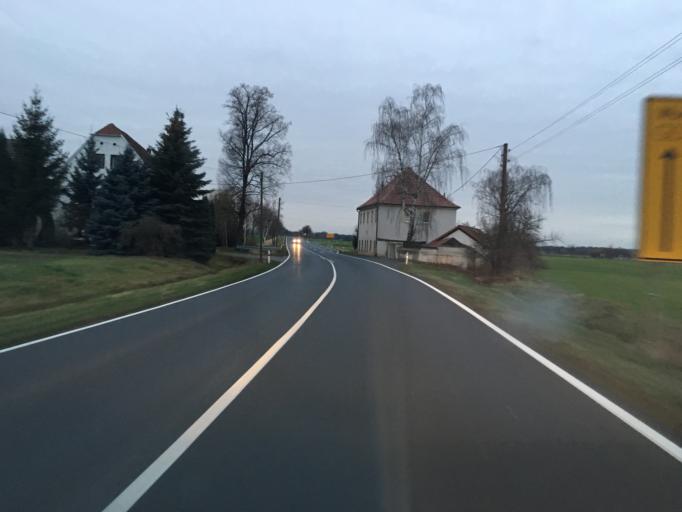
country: DE
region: Saxony
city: Oschatz
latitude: 51.3181
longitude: 13.0687
